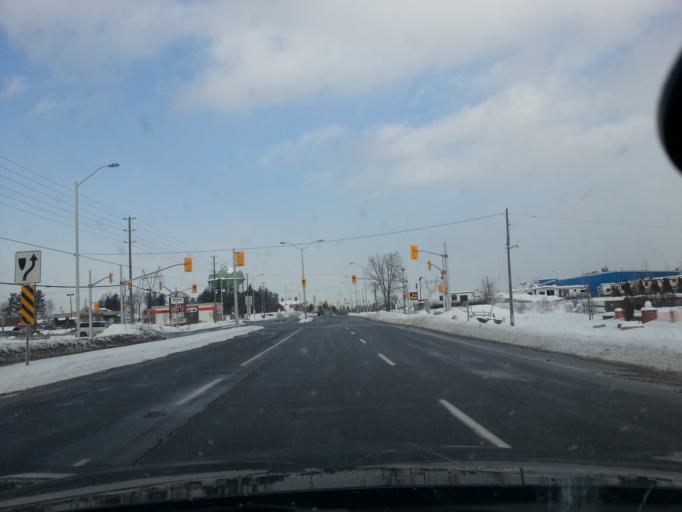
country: CA
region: Ontario
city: Bells Corners
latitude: 45.2658
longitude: -75.9410
